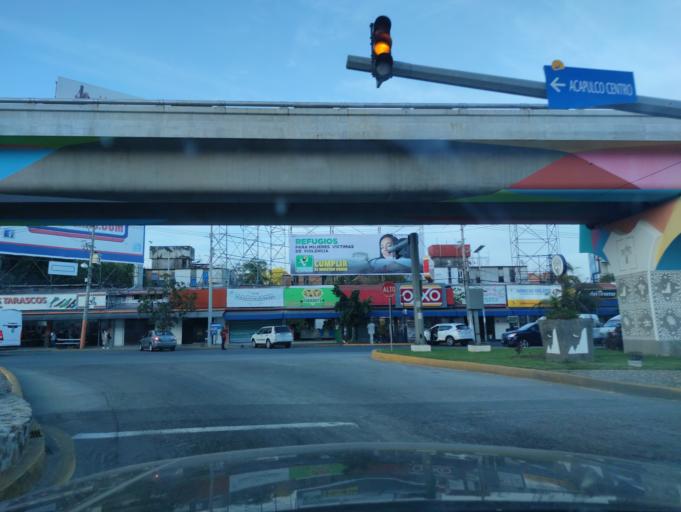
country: MX
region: Guerrero
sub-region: Acapulco de Juarez
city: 10 de Abril
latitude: 16.7713
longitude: -99.7725
